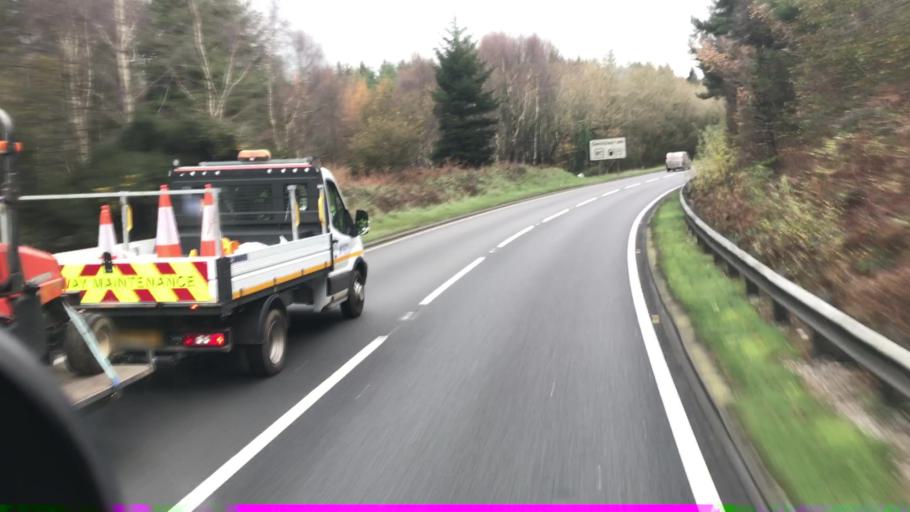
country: GB
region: England
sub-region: Devon
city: Chudleigh
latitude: 50.6358
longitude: -3.5655
